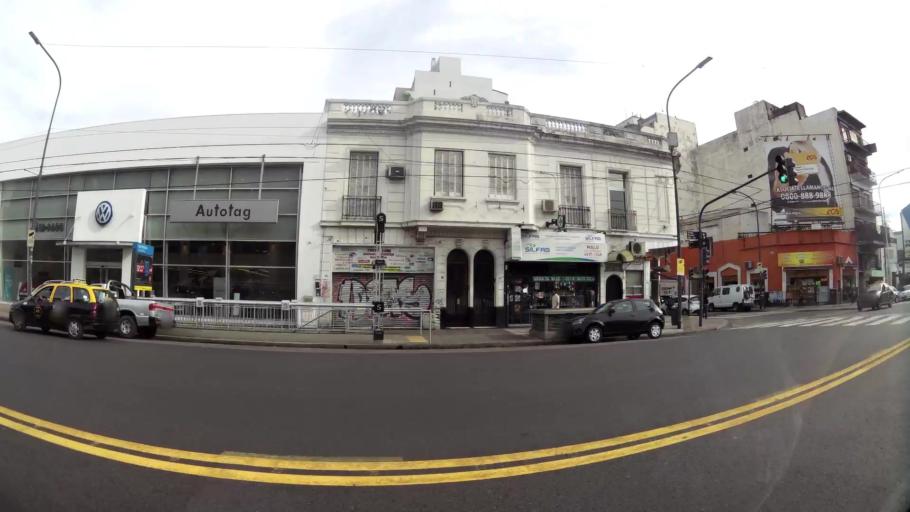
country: AR
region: Buenos Aires F.D.
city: Villa Santa Rita
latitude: -34.6308
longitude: -58.4710
